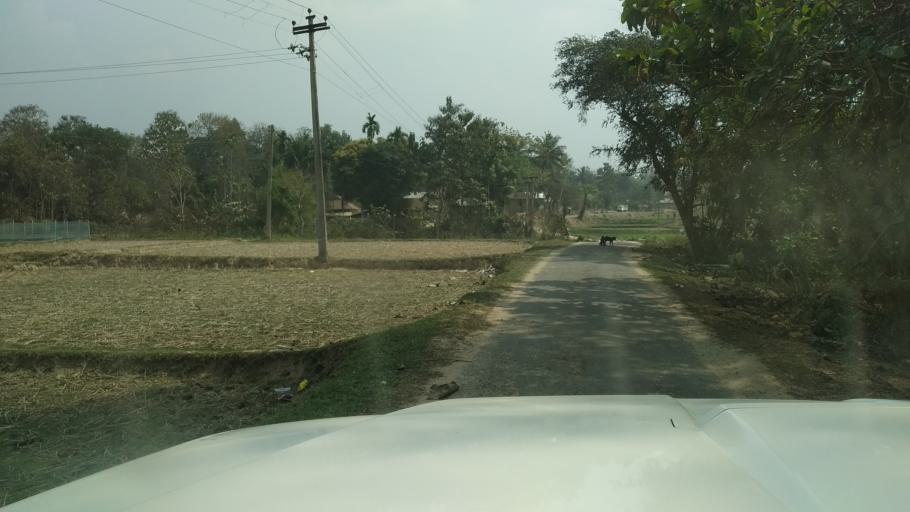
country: IN
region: Tripura
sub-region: West Tripura
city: Sonamura
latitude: 23.4283
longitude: 91.3191
